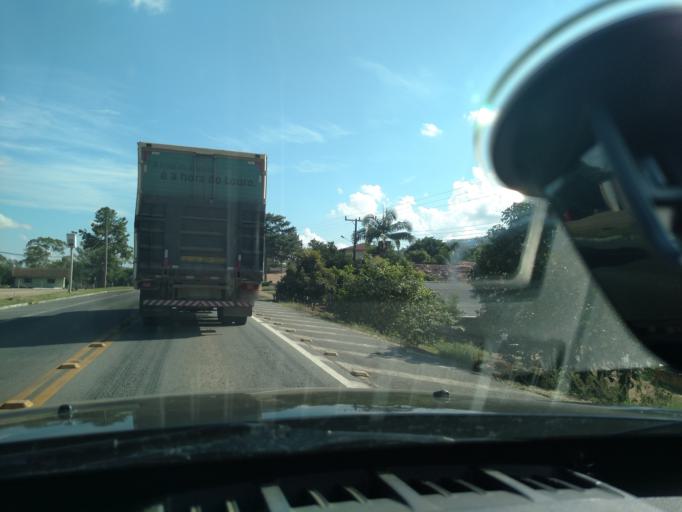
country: BR
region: Santa Catarina
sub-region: Ibirama
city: Ibirama
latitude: -27.1247
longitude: -49.5373
